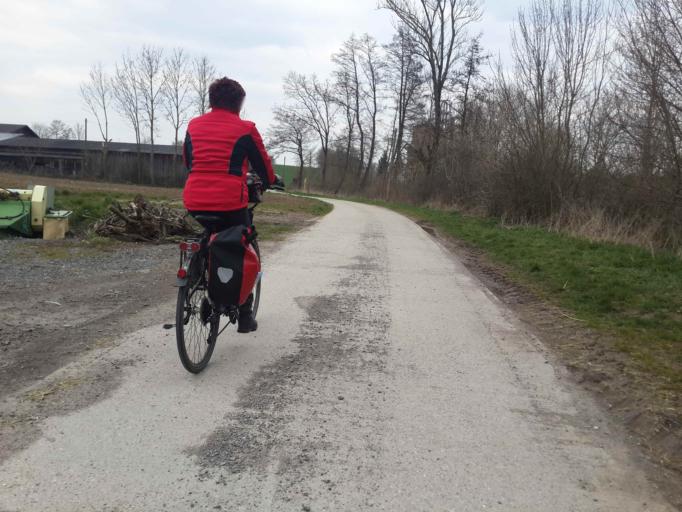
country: DE
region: Baden-Wuerttemberg
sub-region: Regierungsbezirk Stuttgart
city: Ittlingen
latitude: 49.1628
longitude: 8.9381
